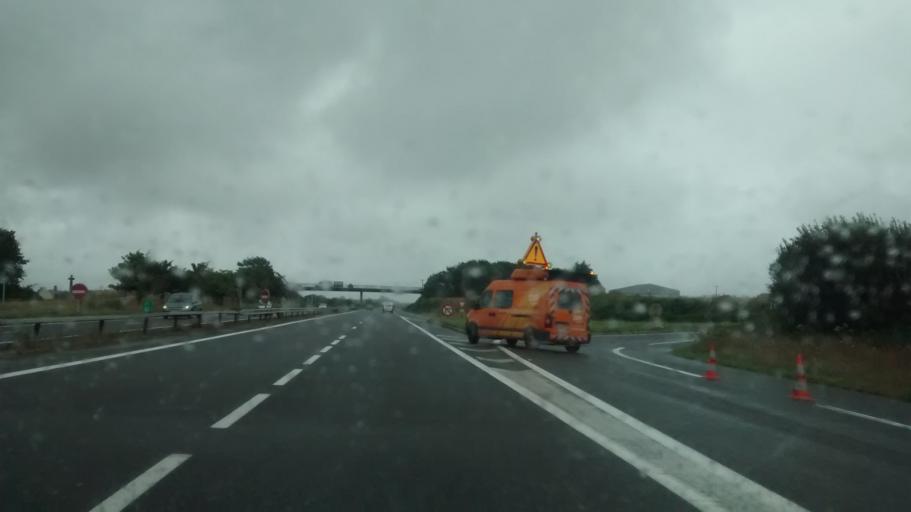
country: FR
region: Brittany
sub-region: Departement du Finistere
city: Plouedern
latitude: 48.4874
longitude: -4.2676
